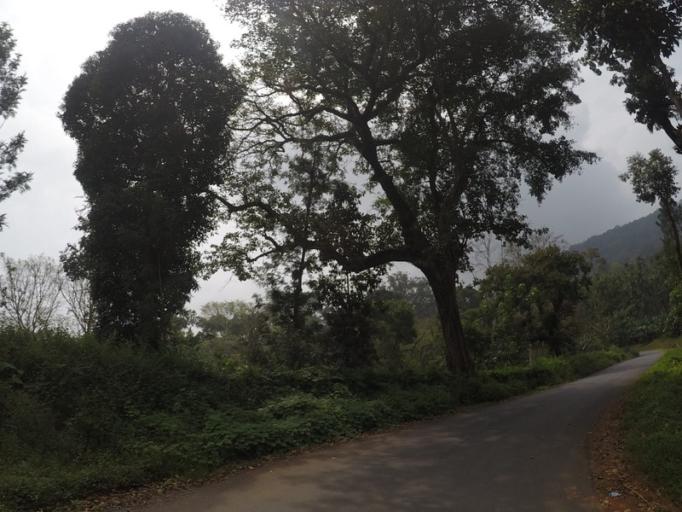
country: IN
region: Karnataka
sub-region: Chikmagalur
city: Mudigere
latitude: 13.1719
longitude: 75.4335
